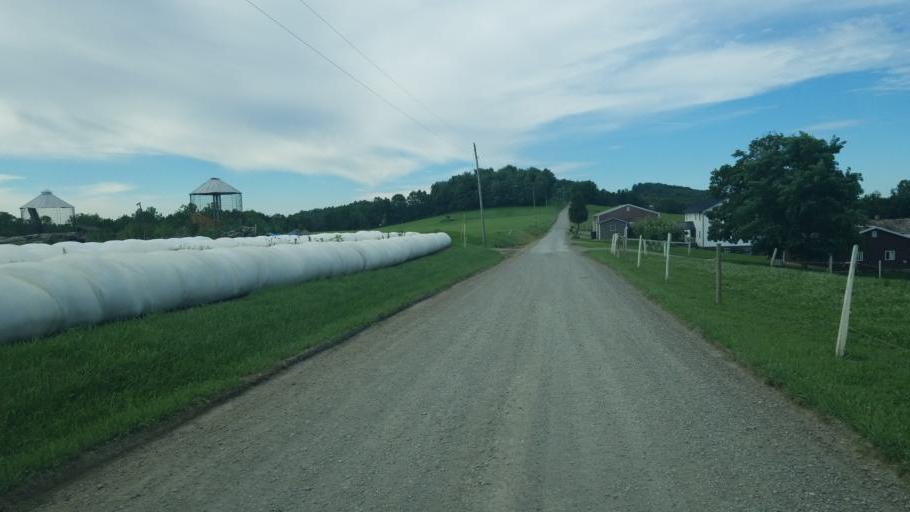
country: US
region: Ohio
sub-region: Holmes County
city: Millersburg
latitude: 40.5106
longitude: -81.8435
